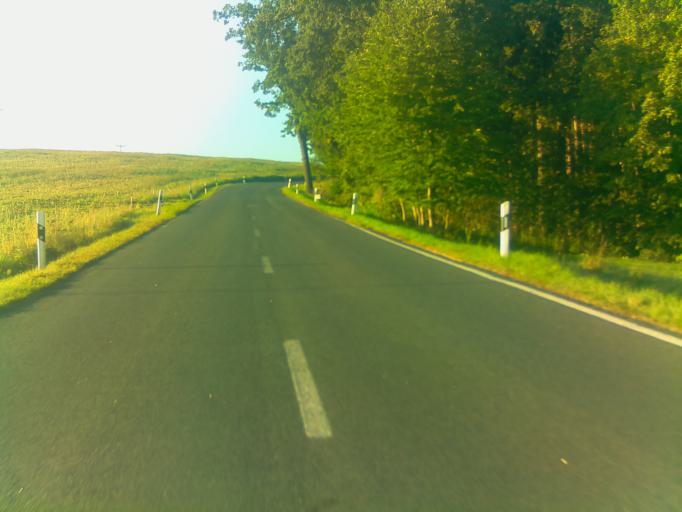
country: DE
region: Thuringia
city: Unterbodnitz
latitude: 50.8109
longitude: 11.6508
